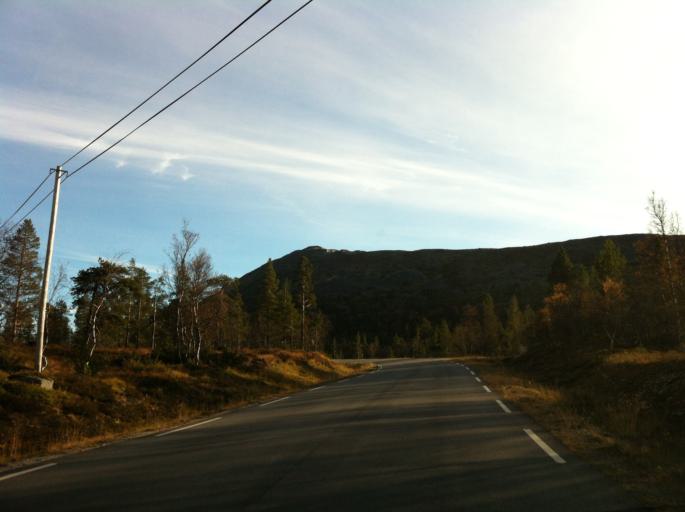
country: NO
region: Hedmark
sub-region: Engerdal
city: Engerdal
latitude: 62.1001
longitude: 12.0287
